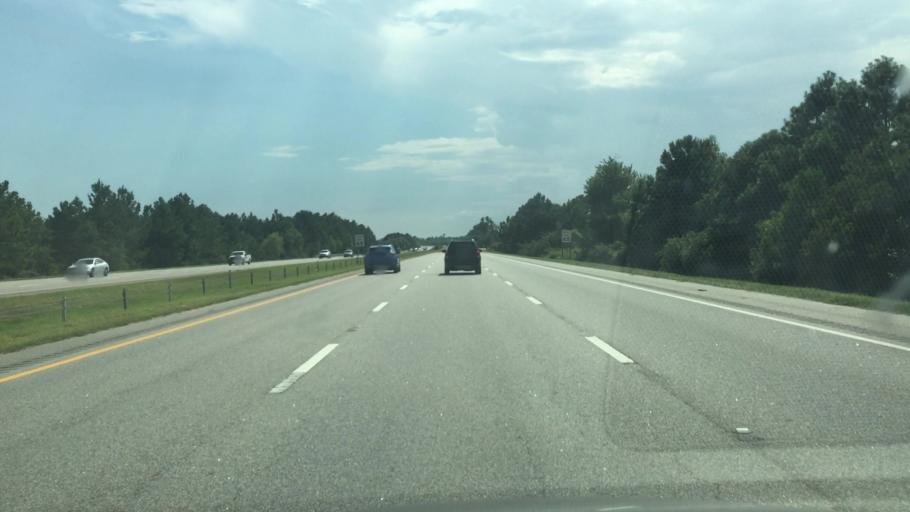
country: US
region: South Carolina
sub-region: Horry County
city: North Myrtle Beach
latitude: 33.8047
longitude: -78.7924
